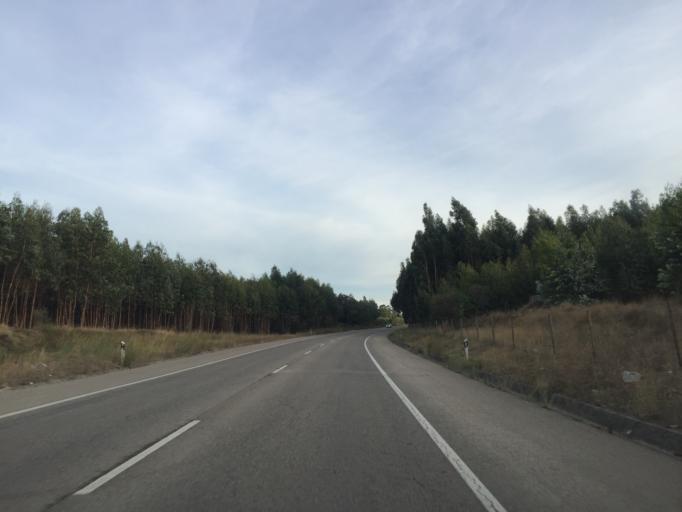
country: PT
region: Leiria
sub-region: Alcobaca
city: Benedita
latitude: 39.4159
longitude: -8.9631
